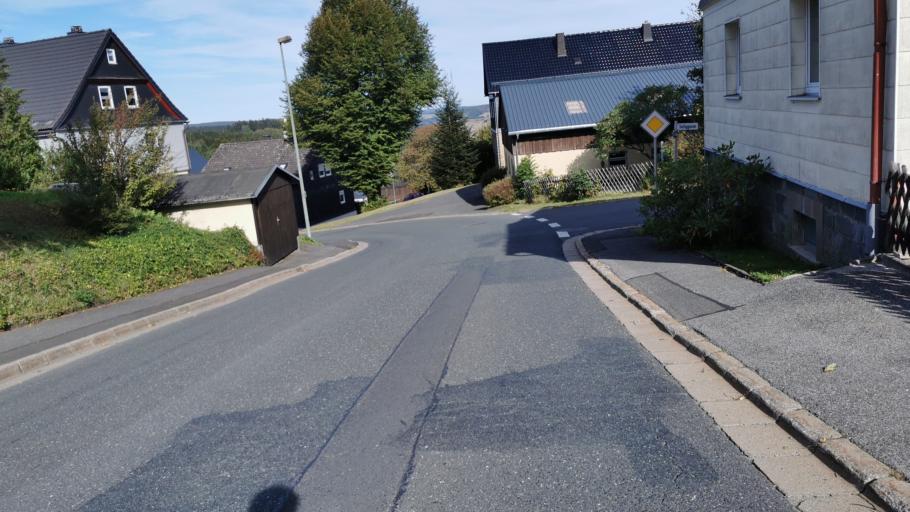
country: DE
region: Bavaria
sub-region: Upper Franconia
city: Ludwigsstadt
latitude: 50.4568
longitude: 11.4033
